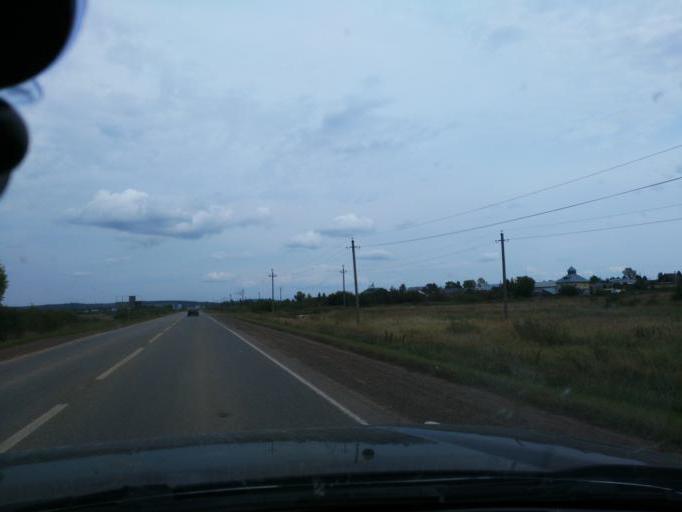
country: RU
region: Perm
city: Kuyeda
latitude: 56.4445
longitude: 55.5866
